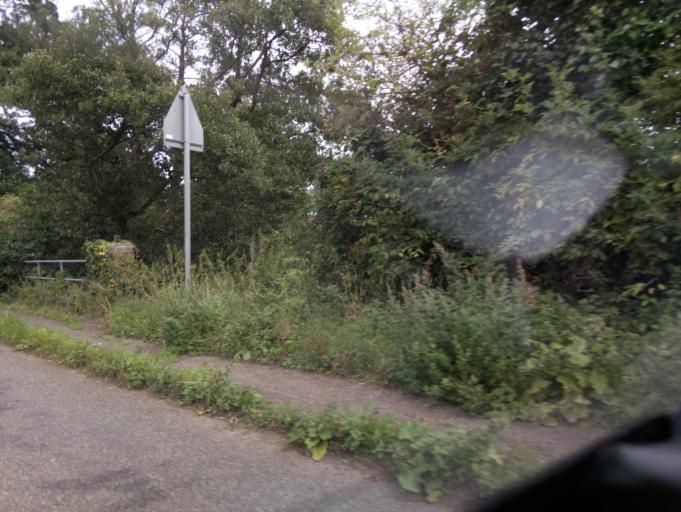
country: GB
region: England
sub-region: Devon
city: Bradninch
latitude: 50.7687
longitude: -3.4424
